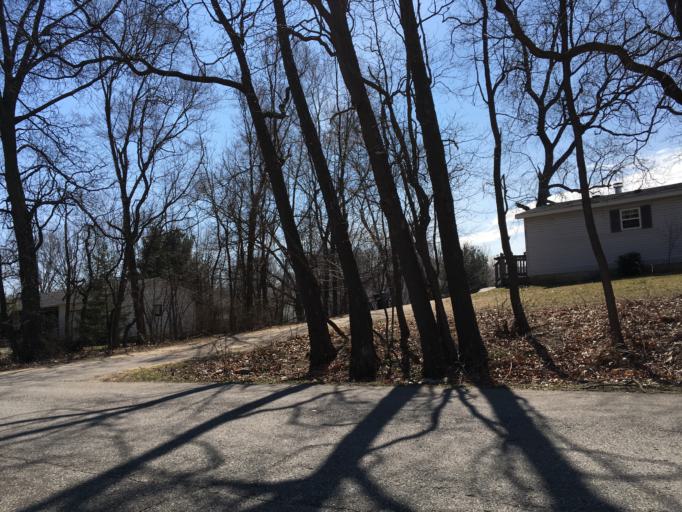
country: US
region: Michigan
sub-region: Kalamazoo County
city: Portage
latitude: 42.1755
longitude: -85.5626
